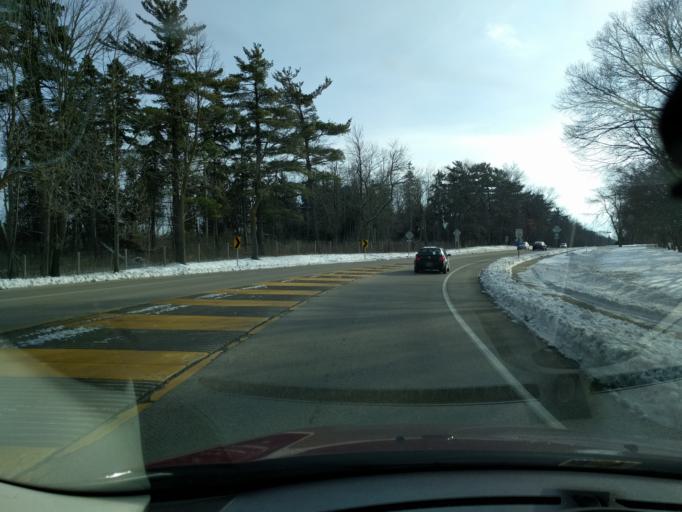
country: US
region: Wisconsin
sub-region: Milwaukee County
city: Bayside
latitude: 43.1760
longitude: -87.8956
